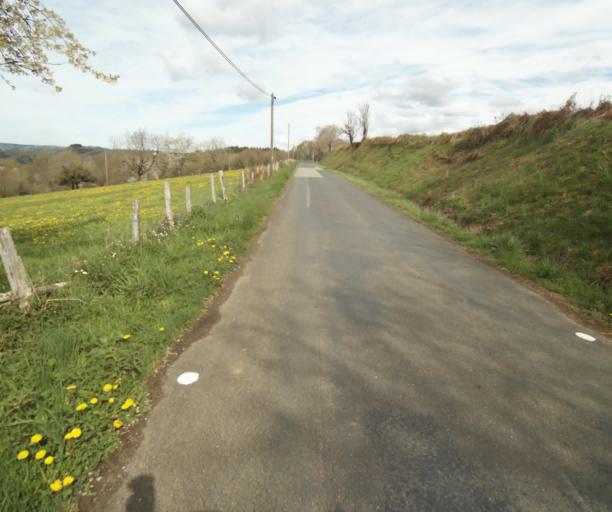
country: FR
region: Limousin
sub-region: Departement de la Correze
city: Laguenne
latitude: 45.2364
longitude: 1.8371
